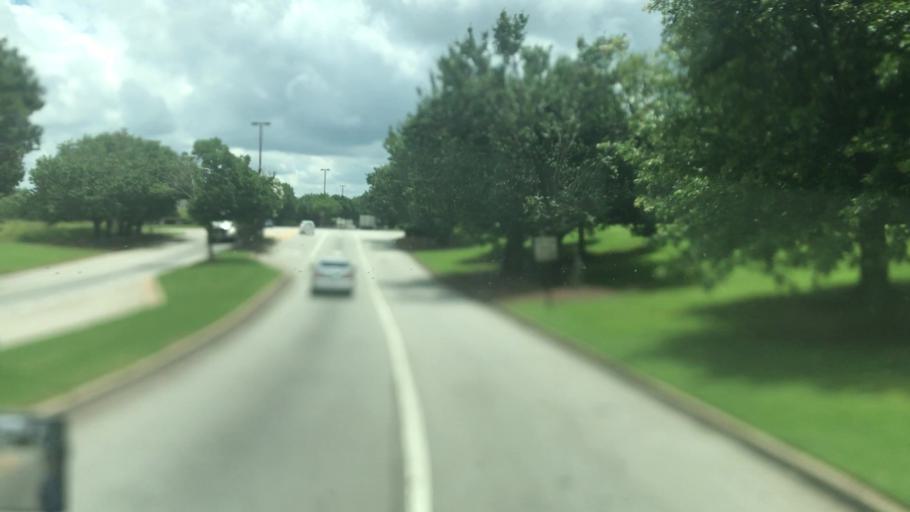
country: US
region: Georgia
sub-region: Henry County
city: McDonough
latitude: 33.4129
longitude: -84.1556
